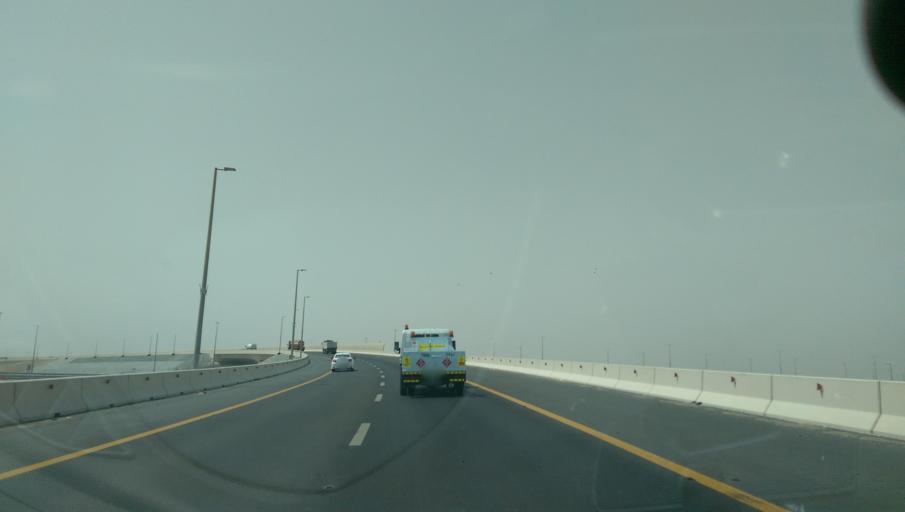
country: AE
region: Abu Dhabi
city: Abu Dhabi
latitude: 24.2888
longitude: 54.5479
